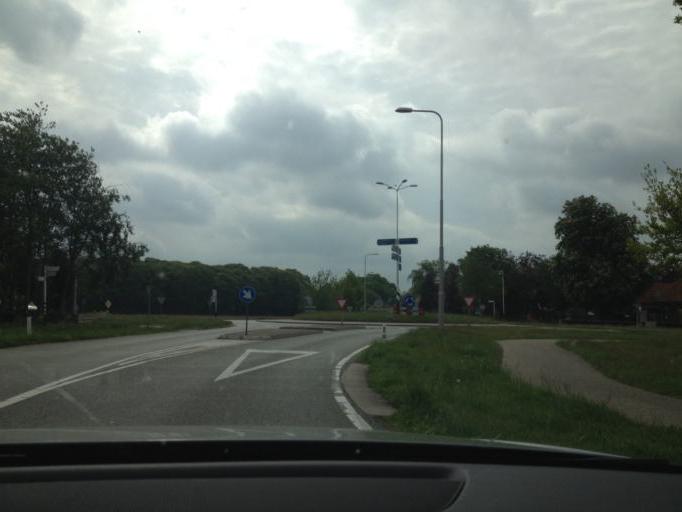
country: NL
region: Gelderland
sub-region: Gemeente Barneveld
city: Terschuur
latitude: 52.1715
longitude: 5.5563
